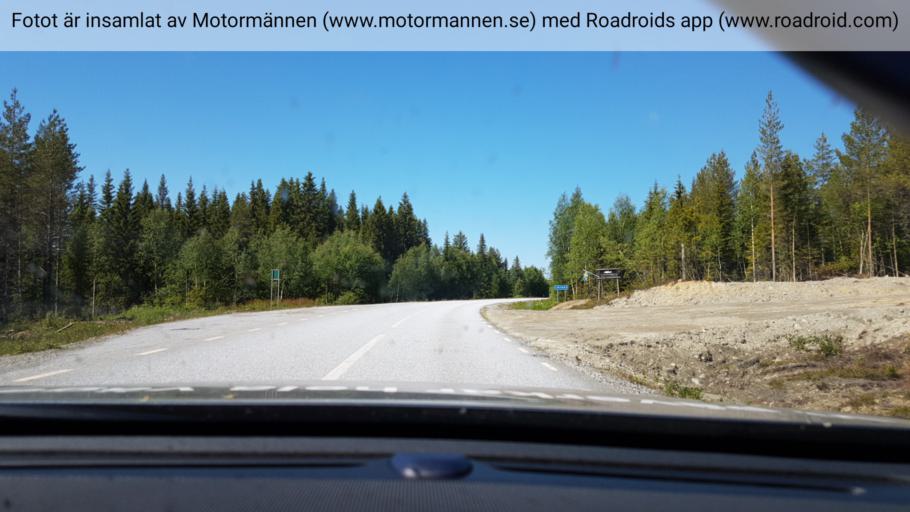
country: SE
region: Vaesterbotten
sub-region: Vilhelmina Kommun
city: Sjoberg
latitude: 64.8366
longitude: 15.9340
